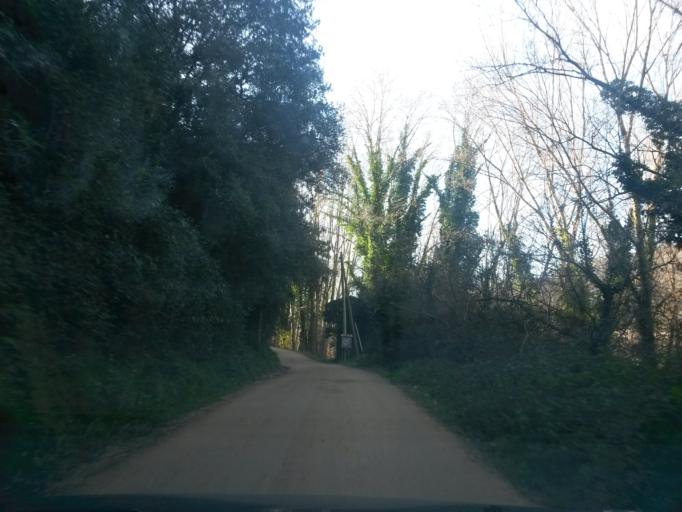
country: ES
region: Catalonia
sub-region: Provincia de Girona
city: la Cellera de Ter
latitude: 41.9754
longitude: 2.6282
